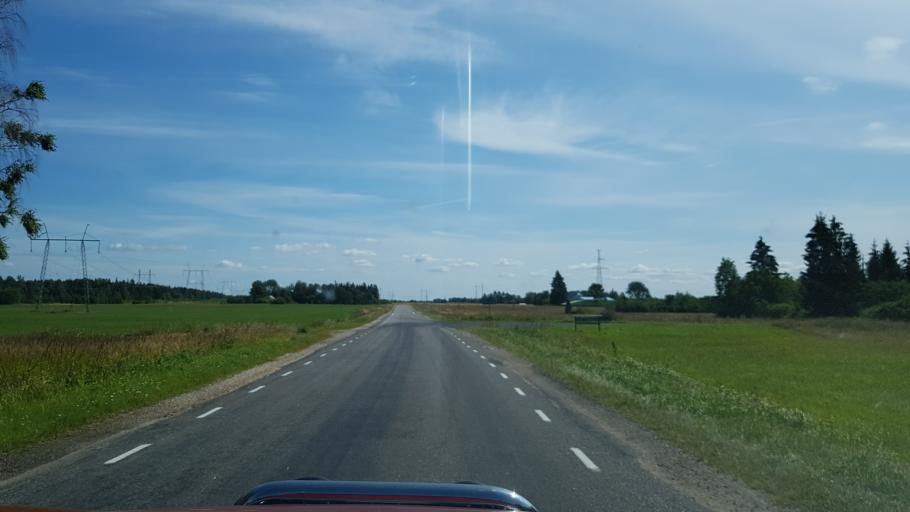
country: EE
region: Laeaene-Virumaa
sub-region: Tapa vald
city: Tapa
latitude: 59.1876
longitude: 25.8609
